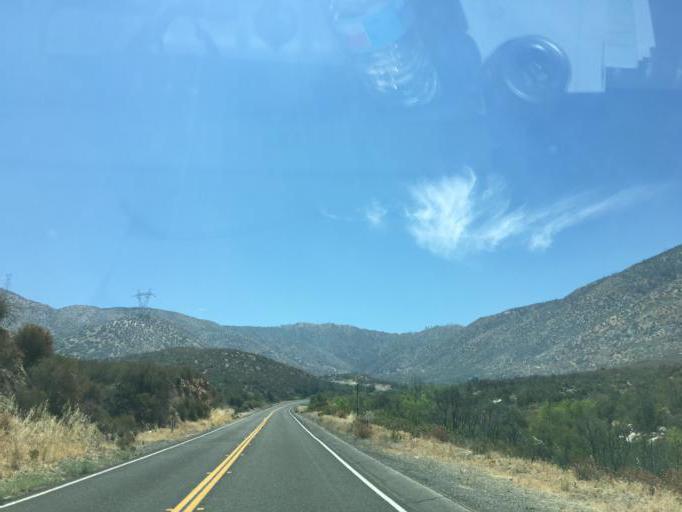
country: US
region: California
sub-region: Los Angeles County
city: Vincent
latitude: 34.4192
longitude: -118.0947
